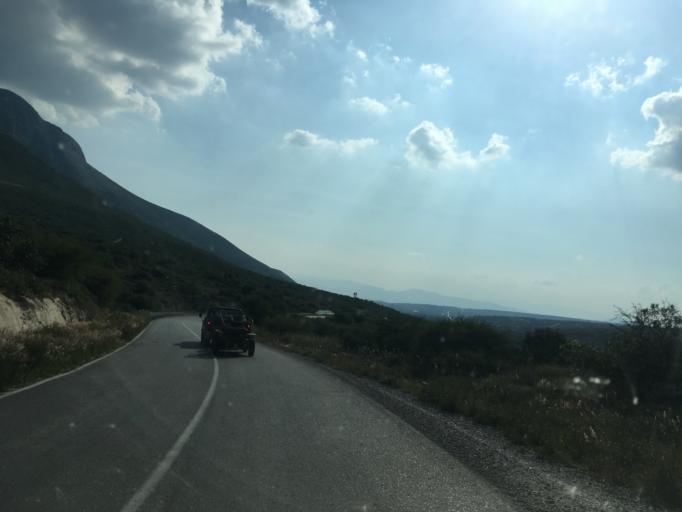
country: MX
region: Hidalgo
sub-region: Cardonal
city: Pozuelos
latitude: 20.6048
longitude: -99.1075
